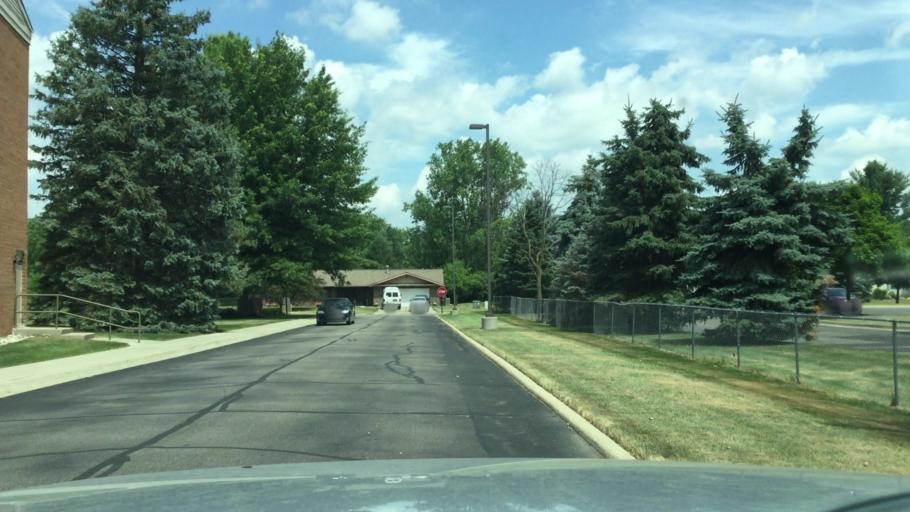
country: US
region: Michigan
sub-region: Genesee County
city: Flushing
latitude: 43.0629
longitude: -83.8158
